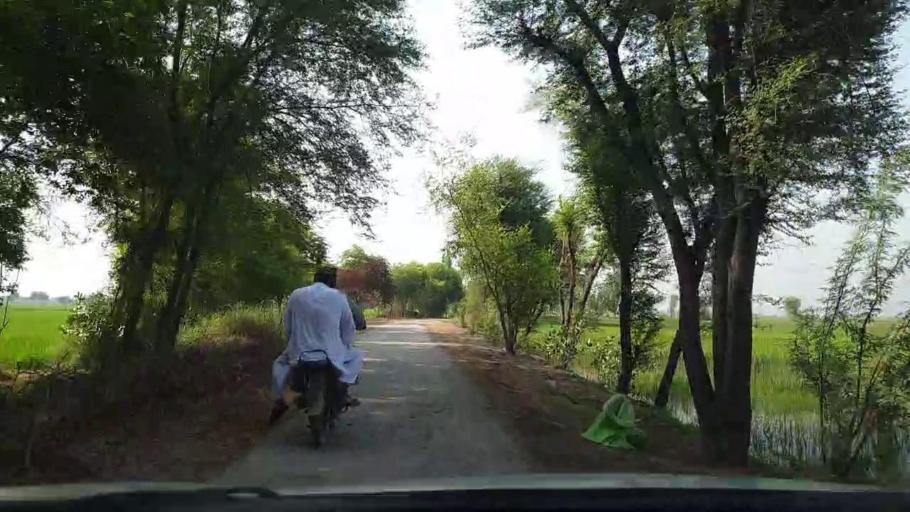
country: PK
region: Sindh
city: Goth Garelo
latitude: 27.4873
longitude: 68.1160
